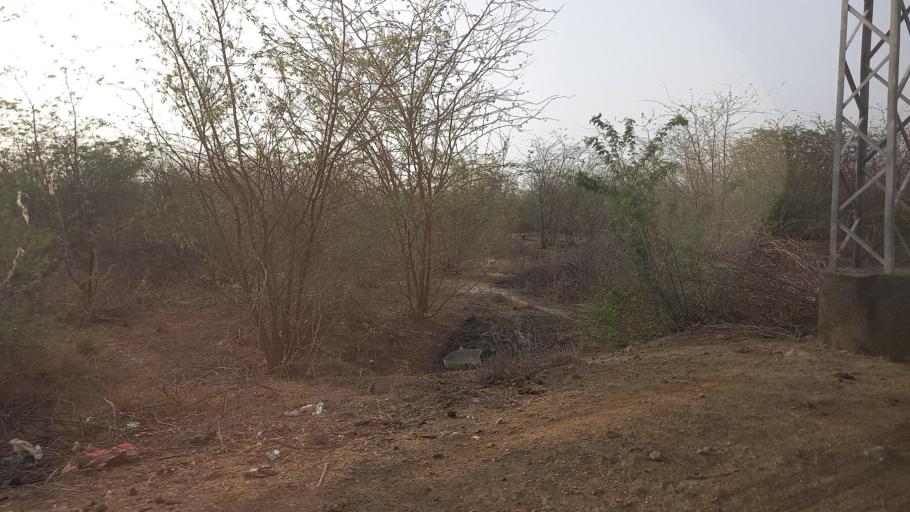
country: PK
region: Sindh
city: Malir Cantonment
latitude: 25.1141
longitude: 67.1915
